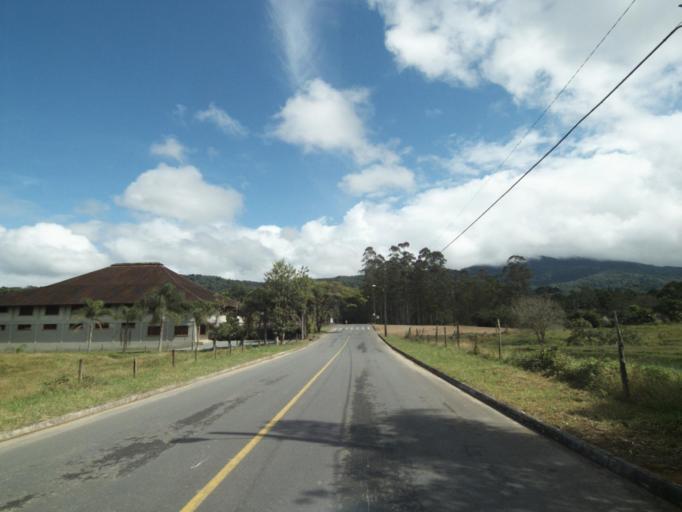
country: BR
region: Santa Catarina
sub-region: Pomerode
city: Pomerode
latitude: -26.6878
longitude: -49.1706
